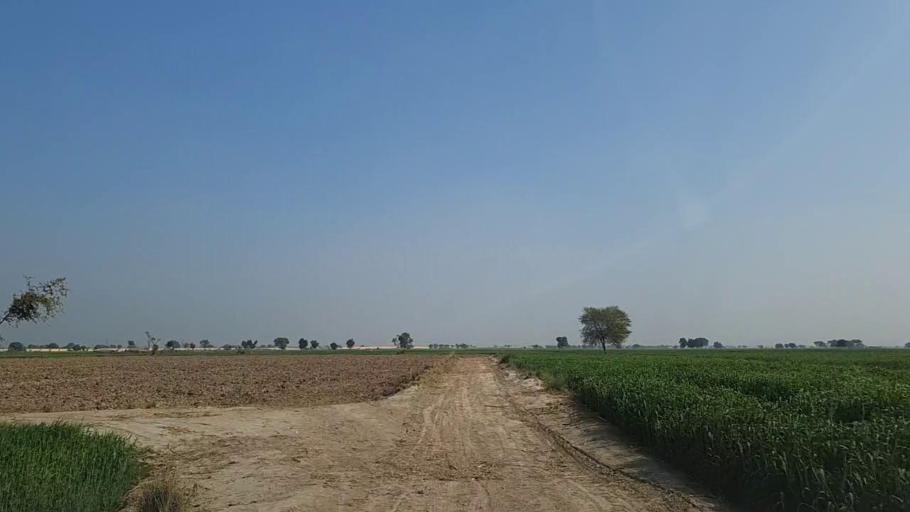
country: PK
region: Sindh
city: Moro
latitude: 26.6809
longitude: 67.9324
